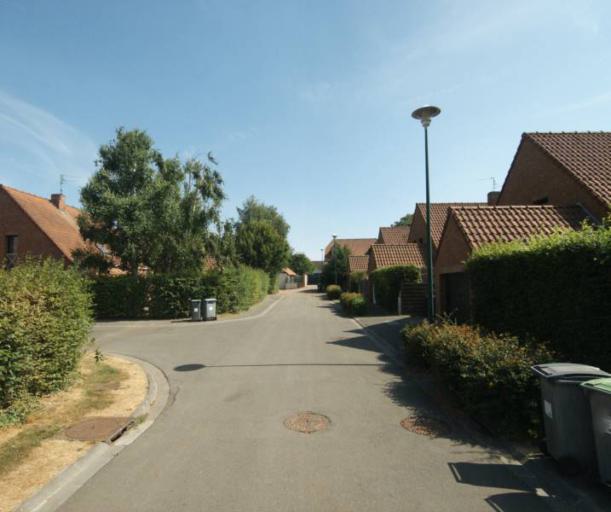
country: FR
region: Nord-Pas-de-Calais
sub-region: Departement du Nord
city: Bondues
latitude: 50.7036
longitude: 3.0849
